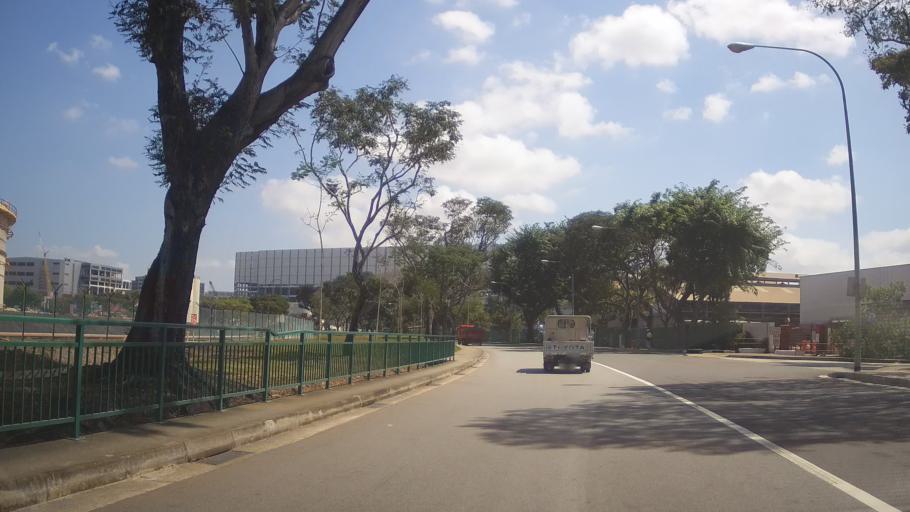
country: SG
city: Singapore
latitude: 1.3043
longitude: 103.6915
